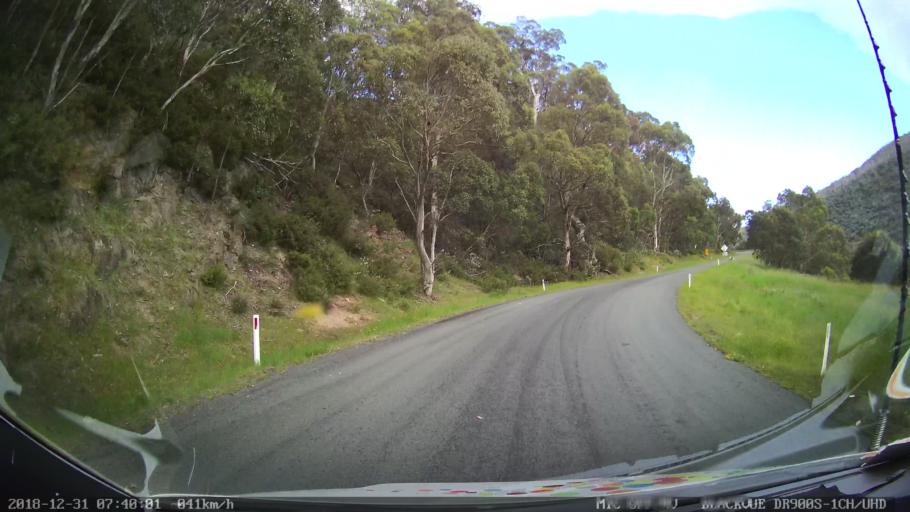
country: AU
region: New South Wales
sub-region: Snowy River
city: Jindabyne
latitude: -36.3506
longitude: 148.4181
